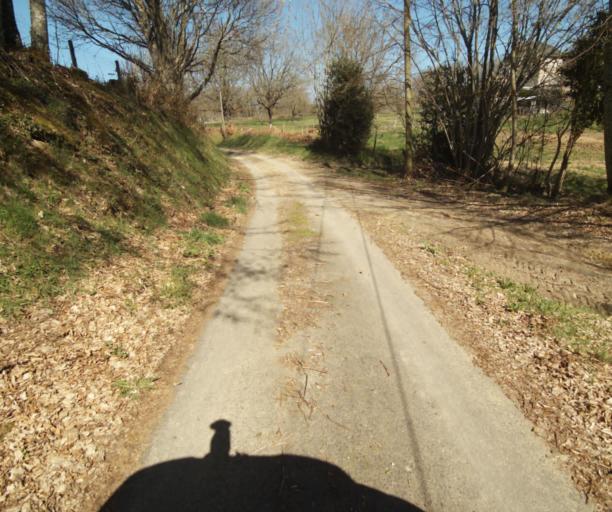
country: FR
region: Limousin
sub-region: Departement de la Correze
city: Saint-Mexant
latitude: 45.2981
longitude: 1.6185
